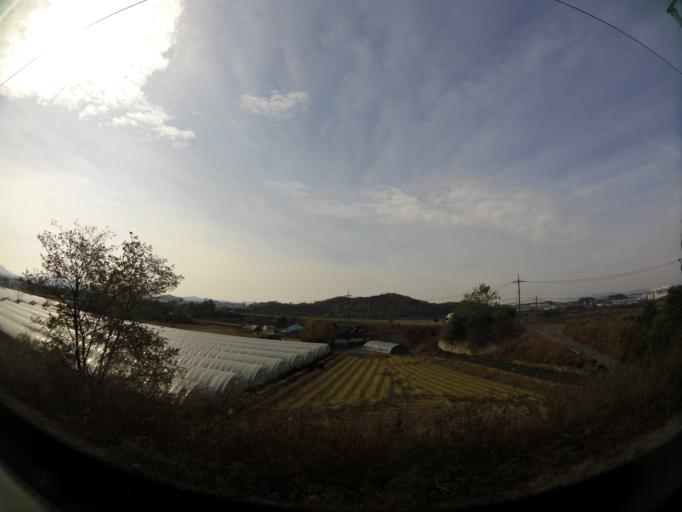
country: KR
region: Daejeon
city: Songgang-dong
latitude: 36.5793
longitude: 127.3093
